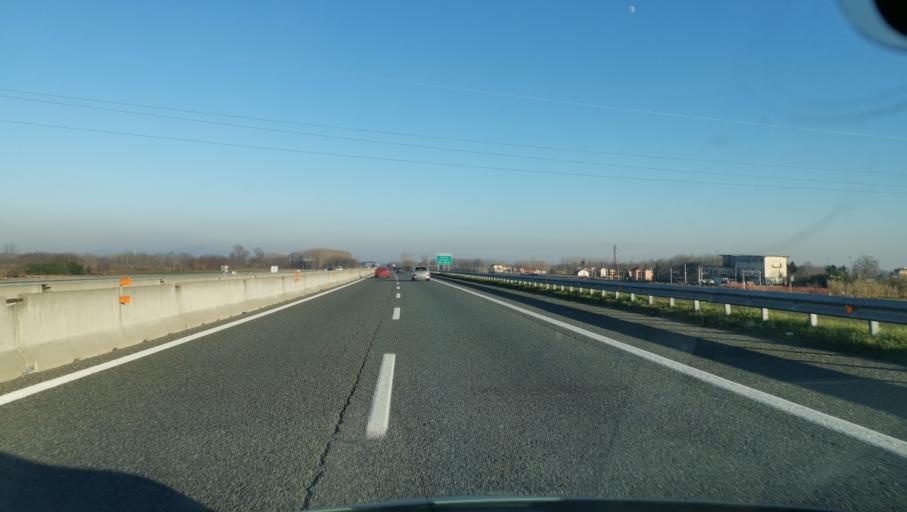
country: IT
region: Piedmont
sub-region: Provincia di Torino
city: Airasca
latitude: 44.9271
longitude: 7.4718
